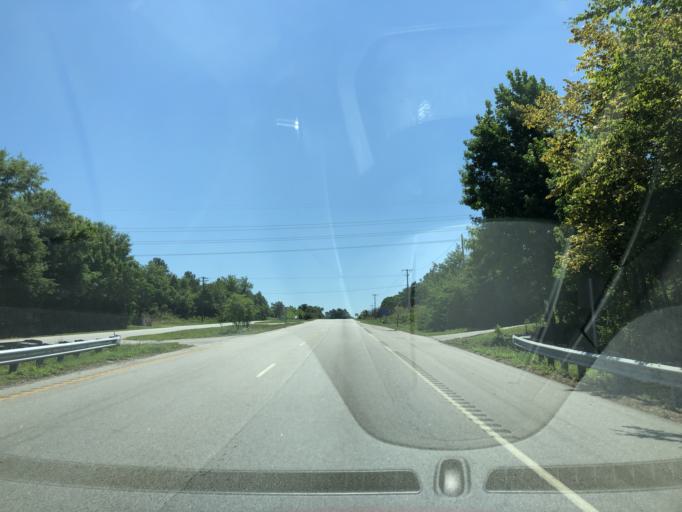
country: US
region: South Carolina
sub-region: Aiken County
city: Clearwater
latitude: 33.4394
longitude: -81.9117
